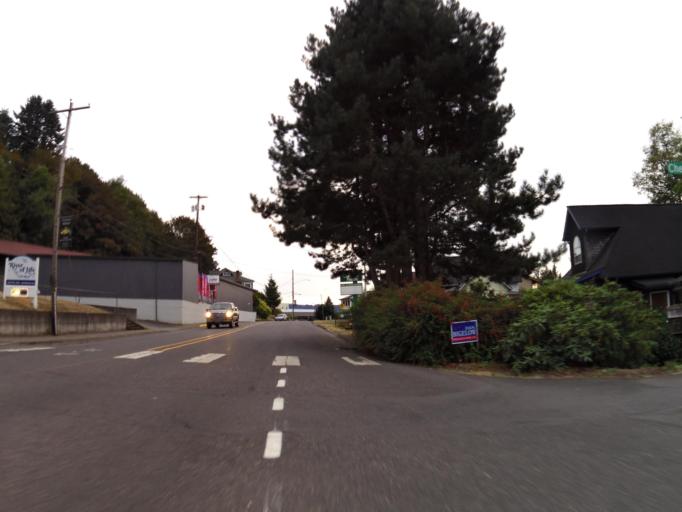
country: US
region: Washington
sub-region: Wahkiakum County
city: Cathlamet
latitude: 46.2034
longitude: -123.3840
